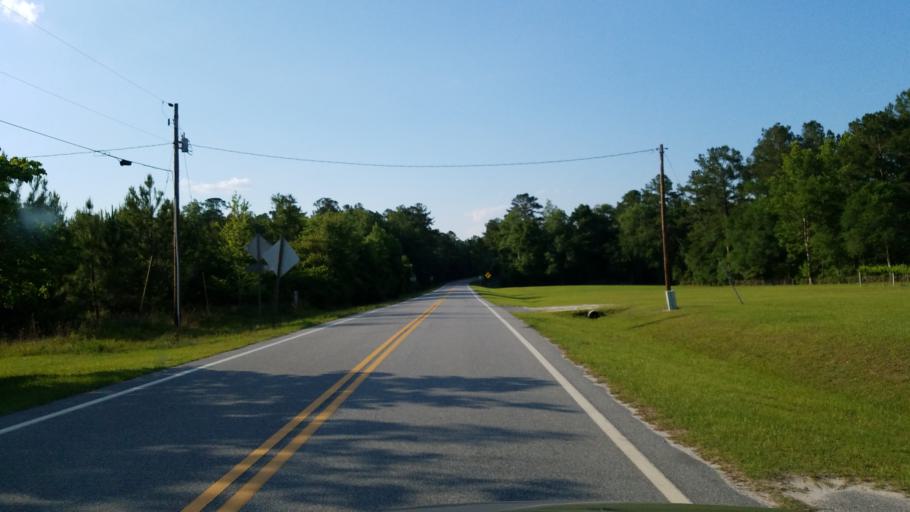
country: US
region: Georgia
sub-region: Echols County
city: Statenville
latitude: 30.8313
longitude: -83.0546
